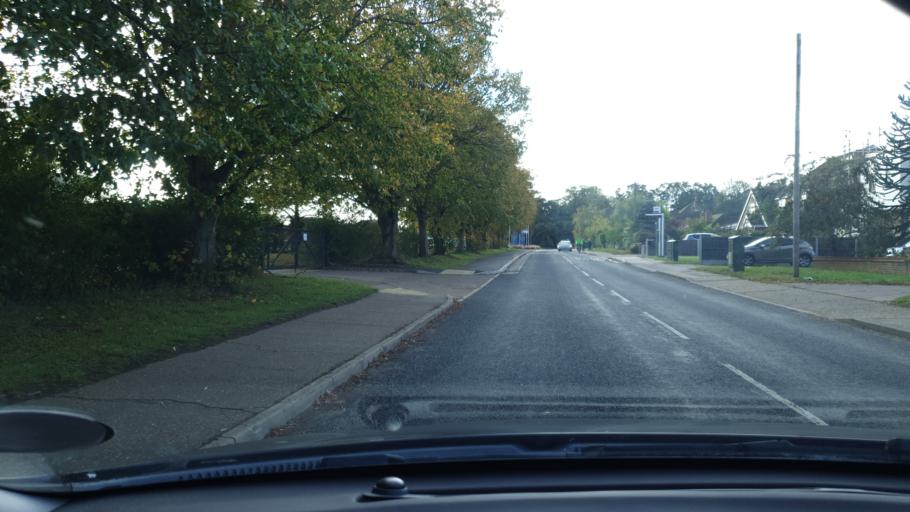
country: GB
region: England
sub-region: Essex
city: Manningtree
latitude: 51.9380
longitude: 1.0439
